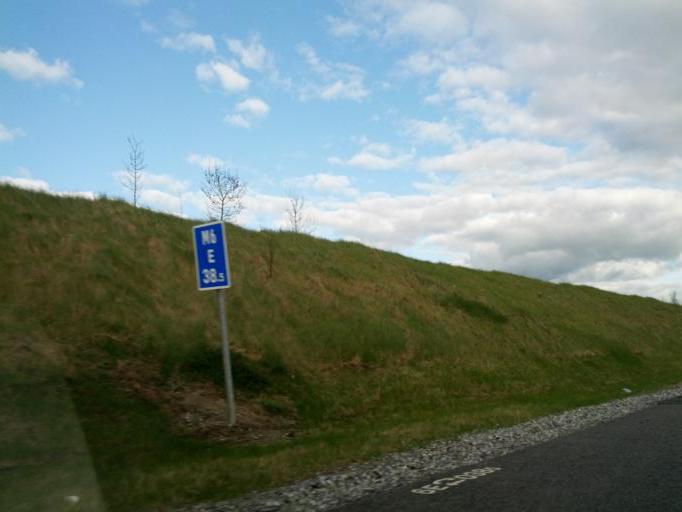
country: IE
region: Leinster
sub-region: Uibh Fhaili
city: Clara
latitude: 53.3907
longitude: -7.6111
